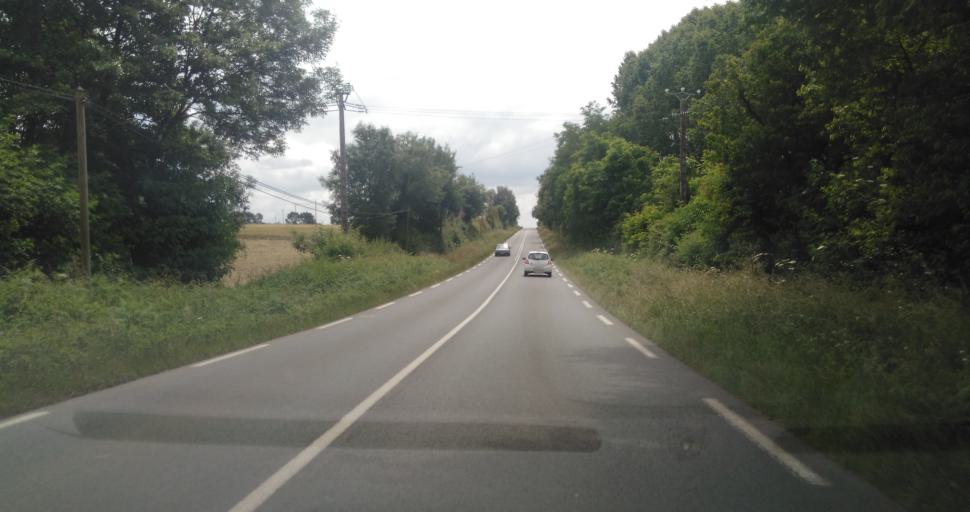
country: FR
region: Pays de la Loire
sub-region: Departement de la Vendee
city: Bournezeau
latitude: 46.6253
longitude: -1.1593
